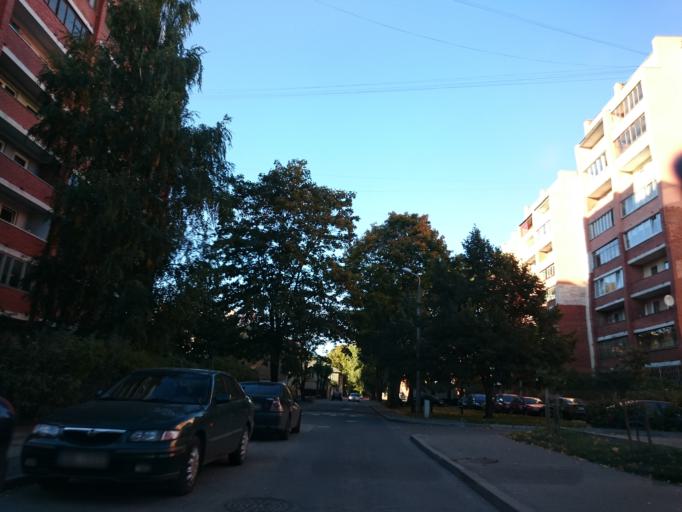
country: LV
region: Riga
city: Jaunciems
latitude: 56.9844
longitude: 24.1709
